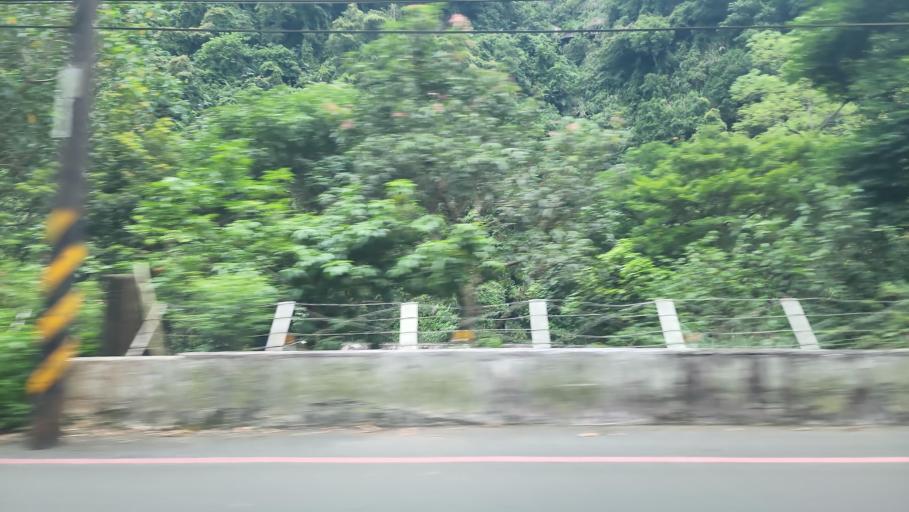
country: TW
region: Taiwan
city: Daxi
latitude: 24.8587
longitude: 121.4350
